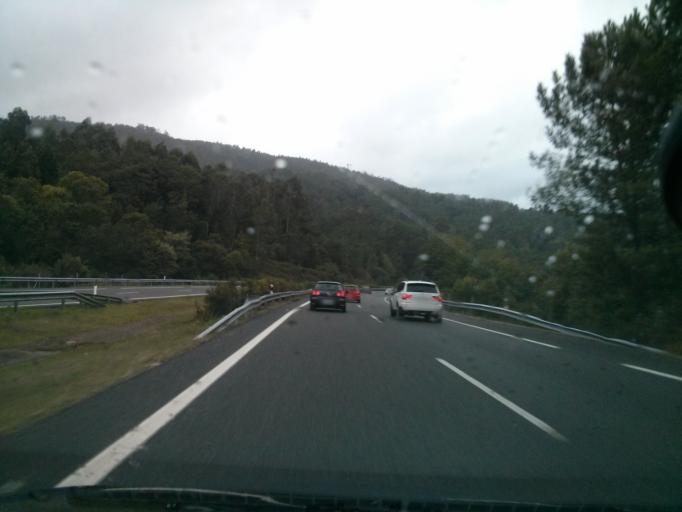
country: ES
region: Galicia
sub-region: Provincia de Pontevedra
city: Ponteareas
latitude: 42.1717
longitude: -8.5487
